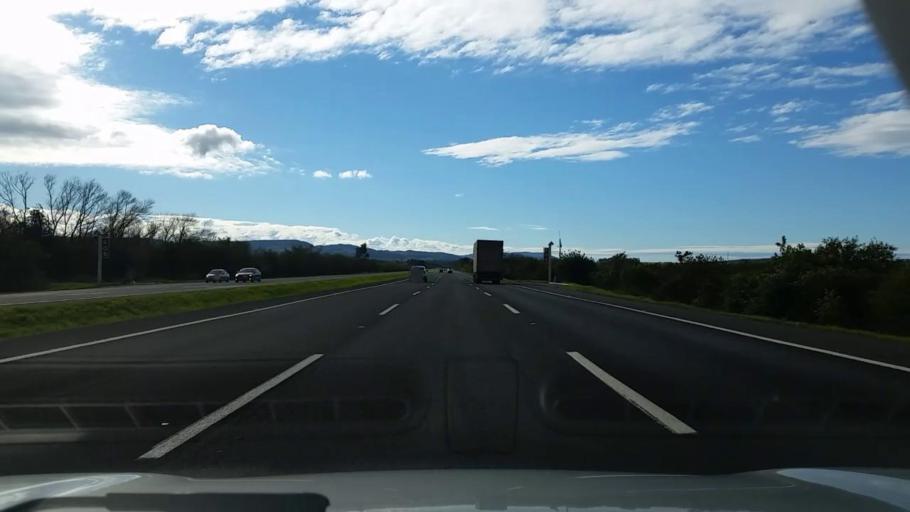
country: BR
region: Rio Grande do Sul
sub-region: Rolante
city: Rolante
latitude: -29.8827
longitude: -50.5334
